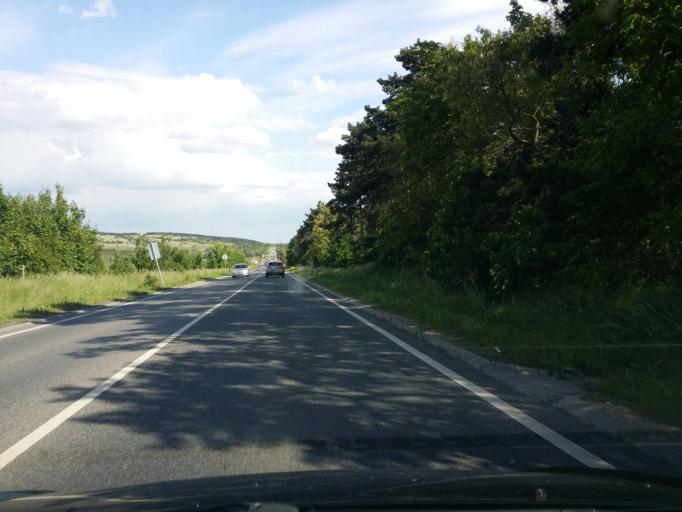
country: HU
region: Veszprem
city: Liter
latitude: 47.1042
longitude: 18.0057
